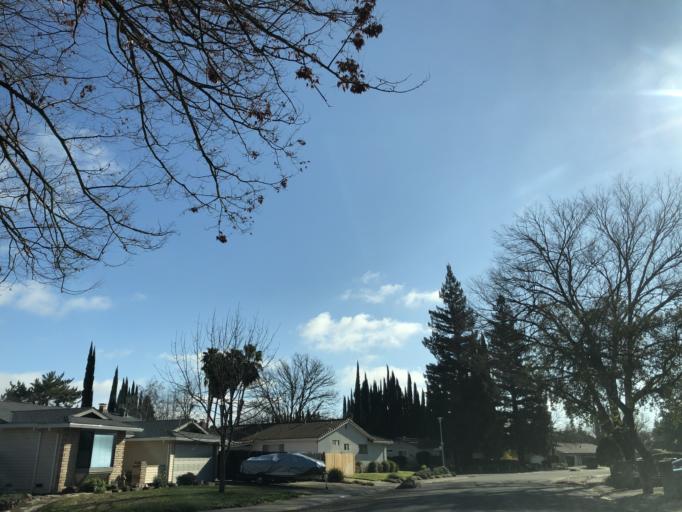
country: US
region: California
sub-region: Sacramento County
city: Rosemont
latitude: 38.5617
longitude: -121.3838
